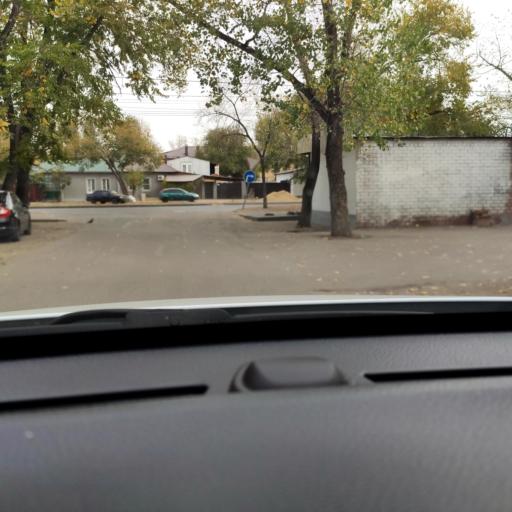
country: RU
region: Voronezj
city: Somovo
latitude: 51.7154
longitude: 39.2740
